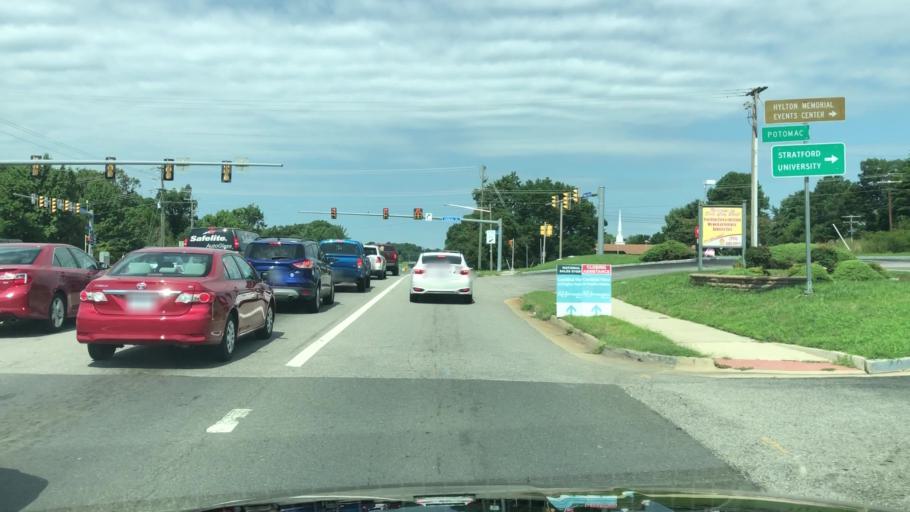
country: US
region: Virginia
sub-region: Prince William County
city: Dale City
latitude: 38.6274
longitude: -77.3026
